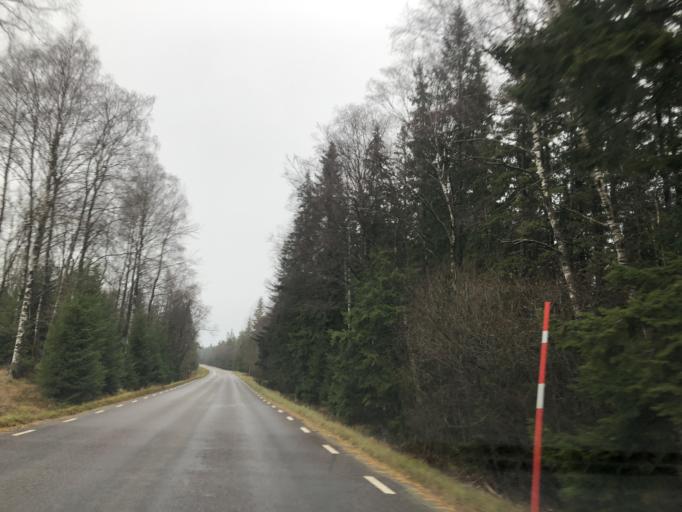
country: SE
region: Vaestra Goetaland
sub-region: Ulricehamns Kommun
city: Ulricehamn
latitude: 57.7546
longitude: 13.5106
